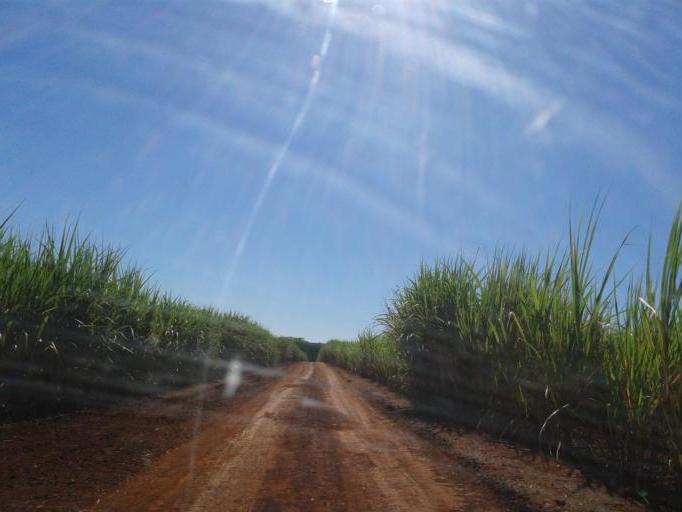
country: BR
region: Minas Gerais
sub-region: Capinopolis
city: Capinopolis
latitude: -18.6796
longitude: -49.6274
